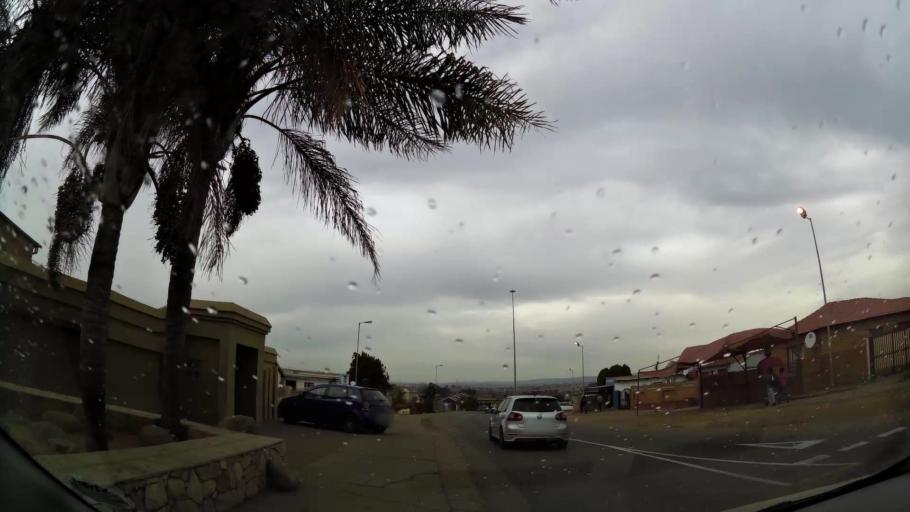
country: ZA
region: Gauteng
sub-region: City of Tshwane Metropolitan Municipality
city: Pretoria
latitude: -25.7155
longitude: 28.3556
